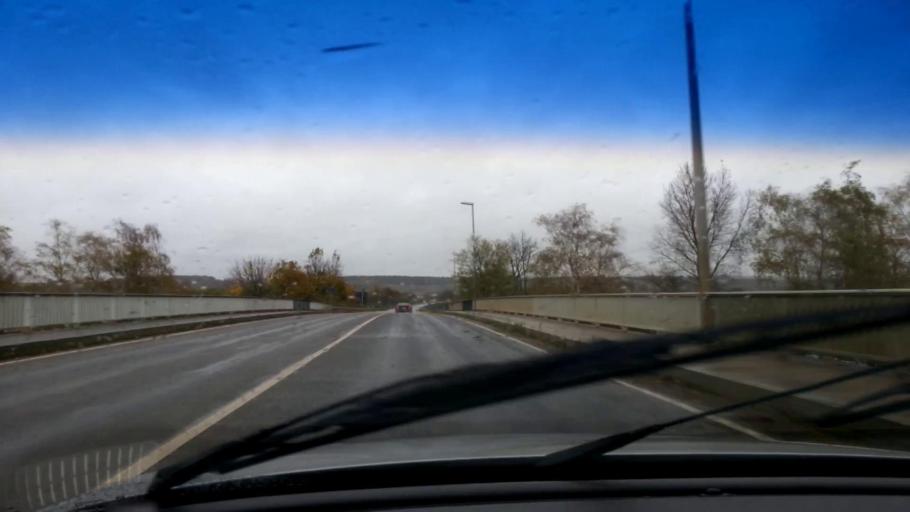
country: DE
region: Bavaria
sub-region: Upper Franconia
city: Viereth-Trunstadt
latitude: 49.9259
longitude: 10.7733
